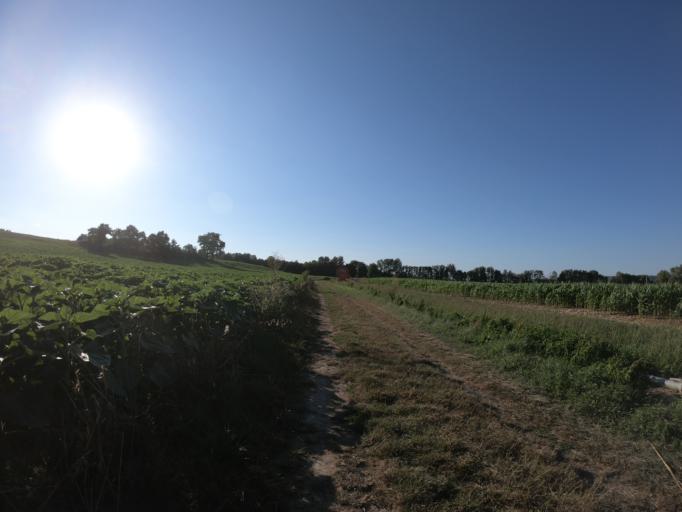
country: FR
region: Midi-Pyrenees
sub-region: Departement de l'Ariege
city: La Tour-du-Crieu
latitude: 43.1037
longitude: 1.7298
